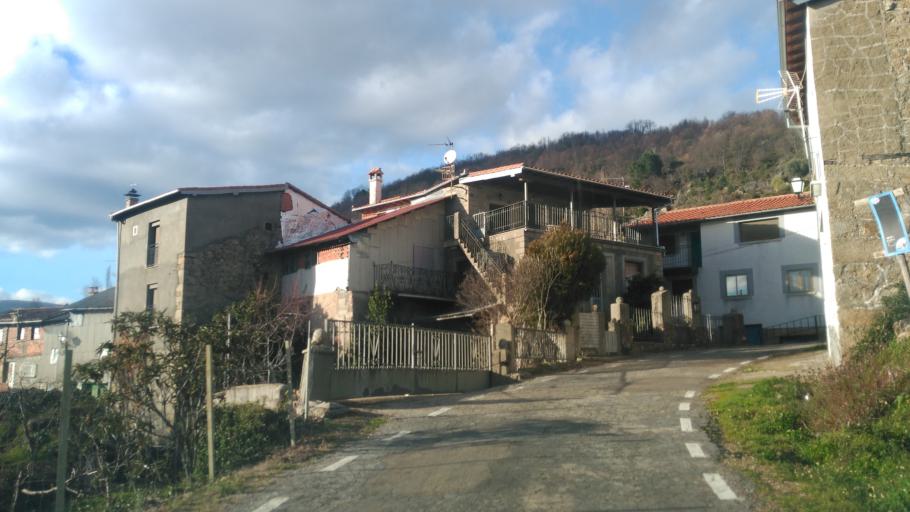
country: ES
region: Castille and Leon
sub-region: Provincia de Salamanca
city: Sequeros
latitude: 40.5054
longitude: -6.0393
